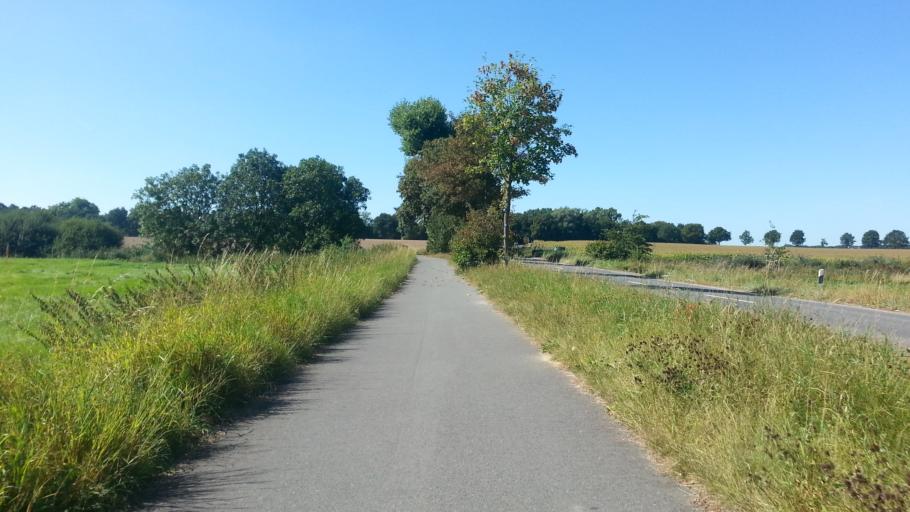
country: DE
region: North Rhine-Westphalia
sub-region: Regierungsbezirk Munster
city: Muenster
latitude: 51.9447
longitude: 7.5742
